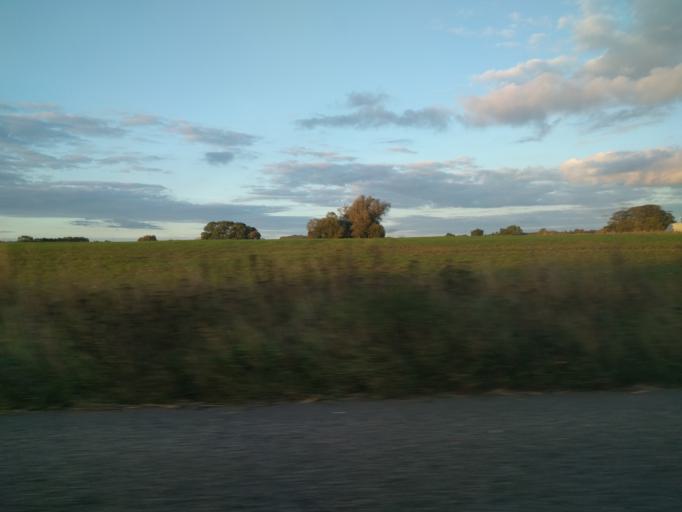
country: DK
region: South Denmark
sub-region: Nyborg Kommune
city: Ullerslev
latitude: 55.3388
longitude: 10.7102
